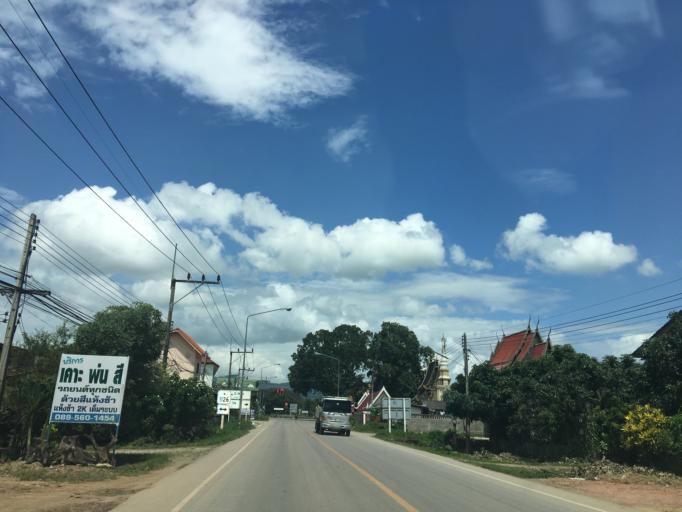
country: TH
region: Chiang Rai
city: Pa Daet
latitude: 19.4996
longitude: 99.9914
